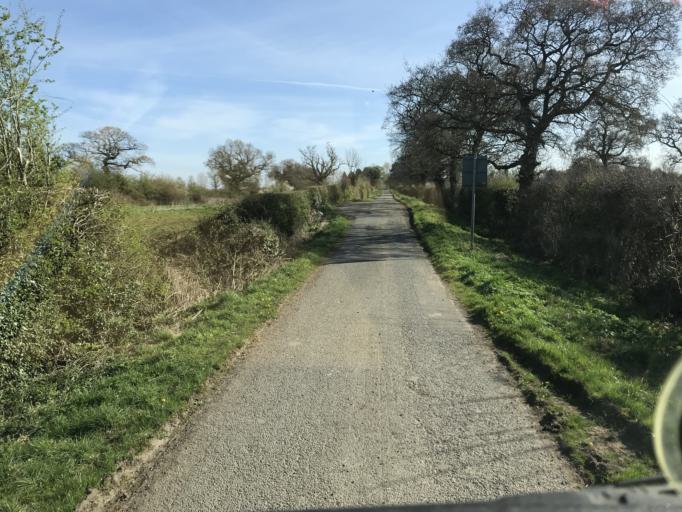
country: GB
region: England
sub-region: Cheshire East
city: Middlewich
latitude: 53.2298
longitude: -2.4688
